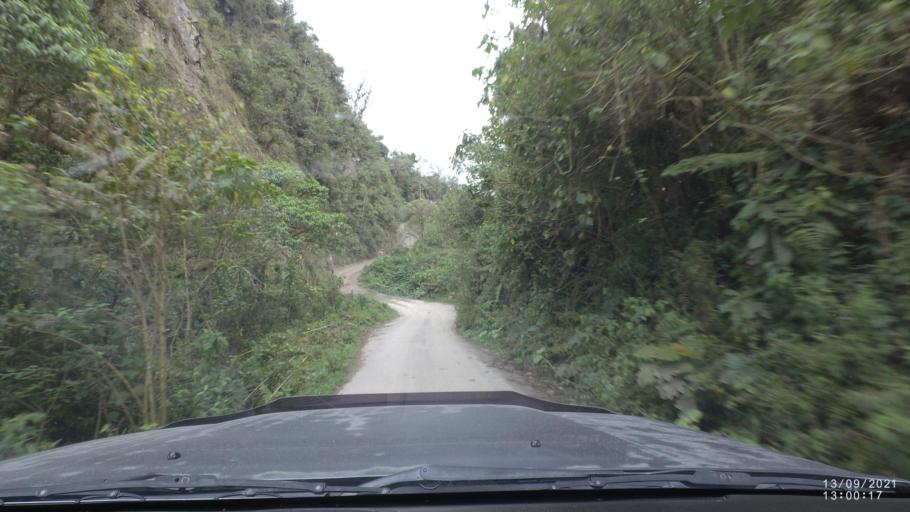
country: BO
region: Cochabamba
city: Colomi
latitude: -17.2355
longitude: -65.8190
